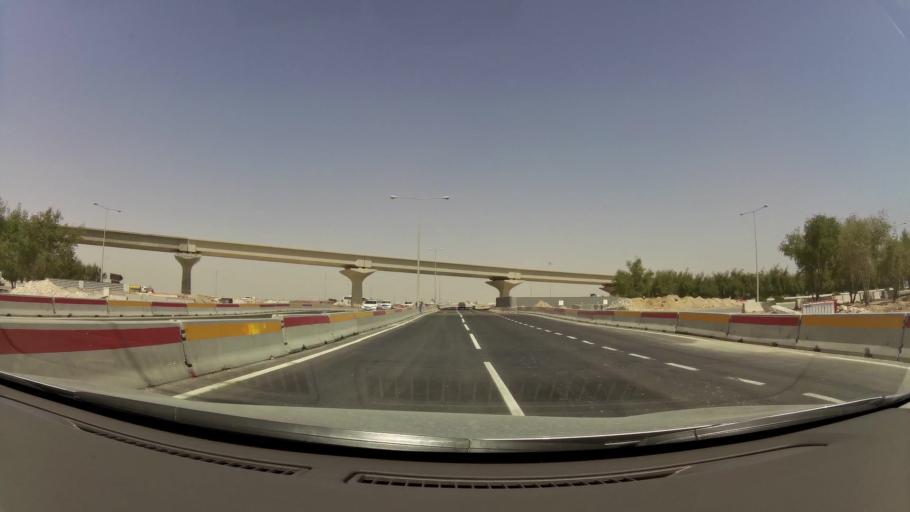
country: QA
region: Baladiyat Umm Salal
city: Umm Salal Muhammad
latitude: 25.3894
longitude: 51.4914
